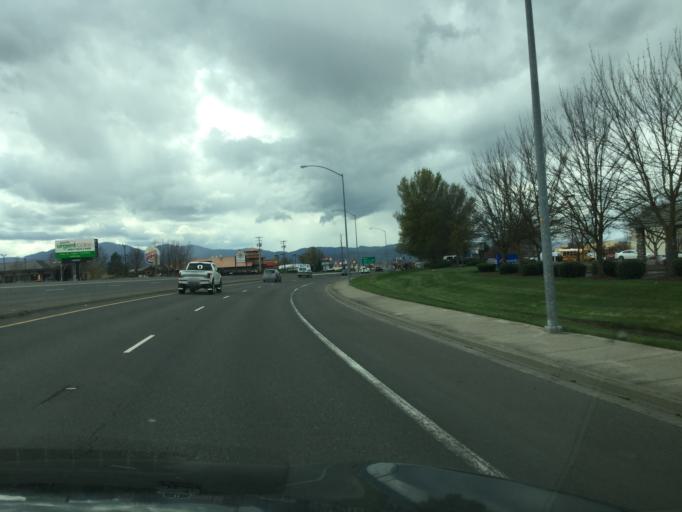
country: US
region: Oregon
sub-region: Jackson County
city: Medford
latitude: 42.3635
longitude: -122.8563
